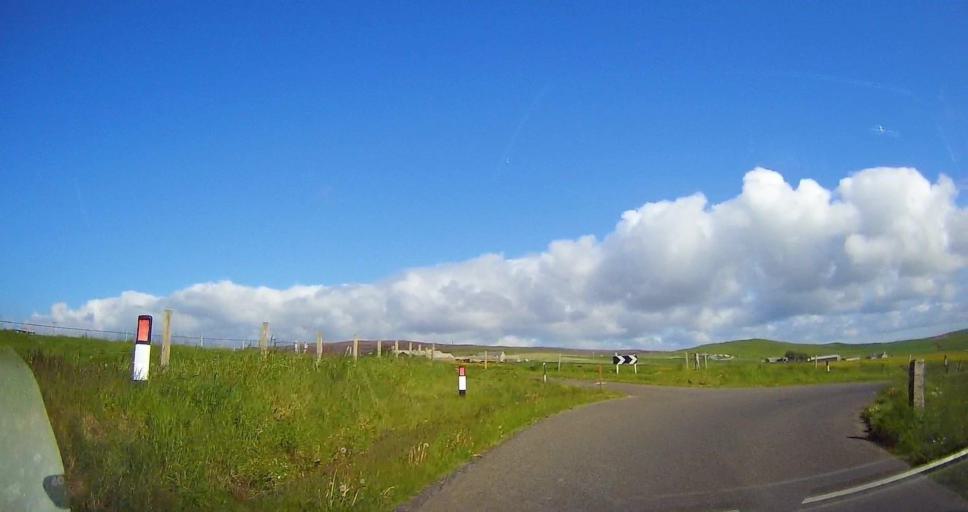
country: GB
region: Scotland
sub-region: Orkney Islands
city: Stromness
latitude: 58.9870
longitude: -3.1471
